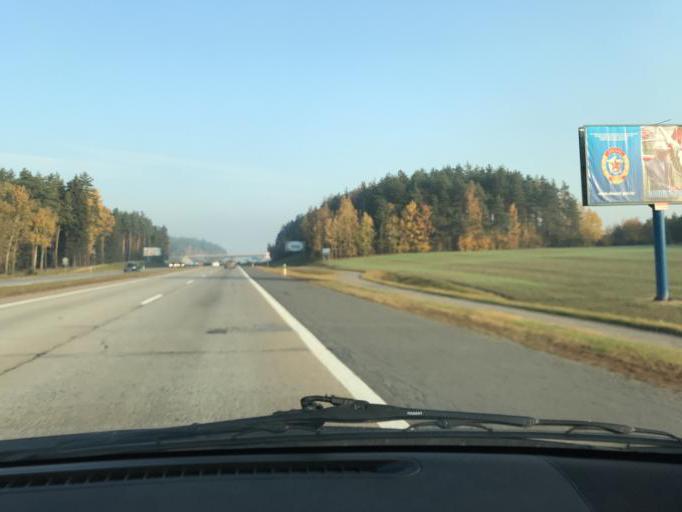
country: BY
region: Minsk
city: Borovlyany
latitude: 53.9989
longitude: 27.6572
